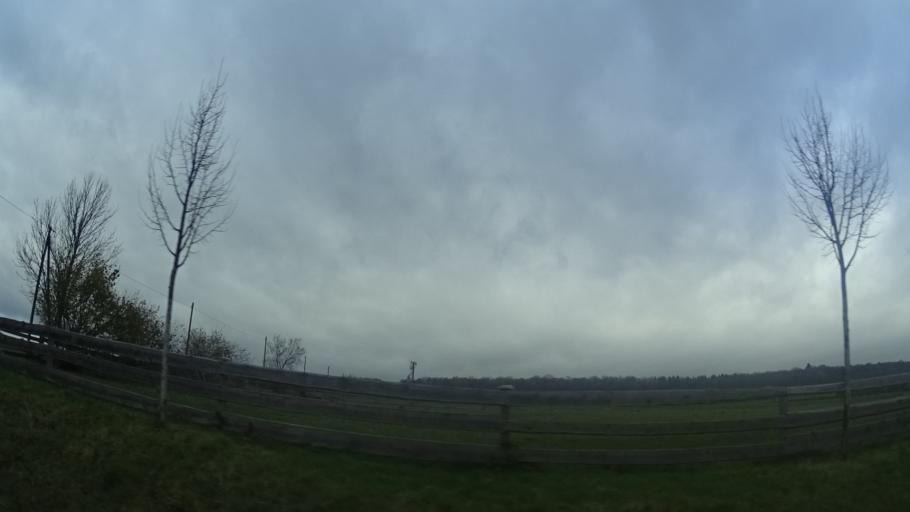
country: DE
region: Thuringia
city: Nauendorf
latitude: 50.9172
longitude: 11.1883
